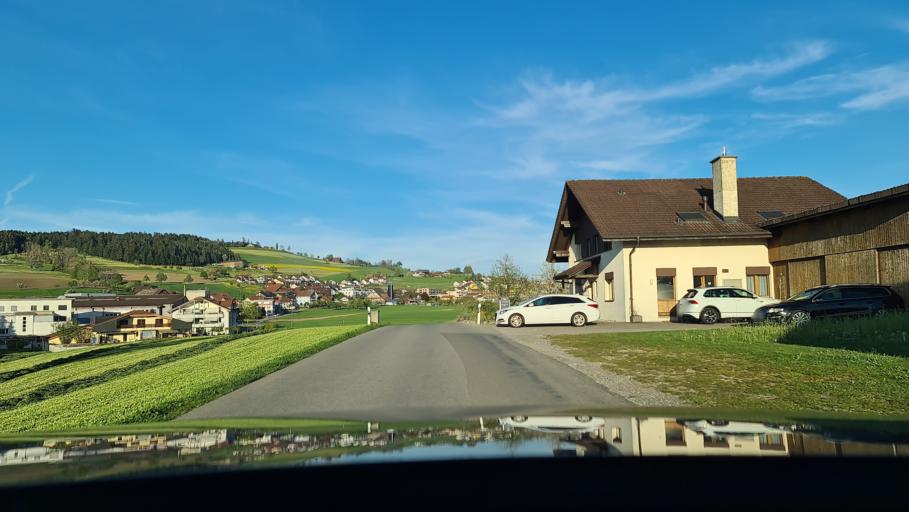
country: CH
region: Lucerne
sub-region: Sursee District
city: Ruswil
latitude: 47.0888
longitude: 8.1020
